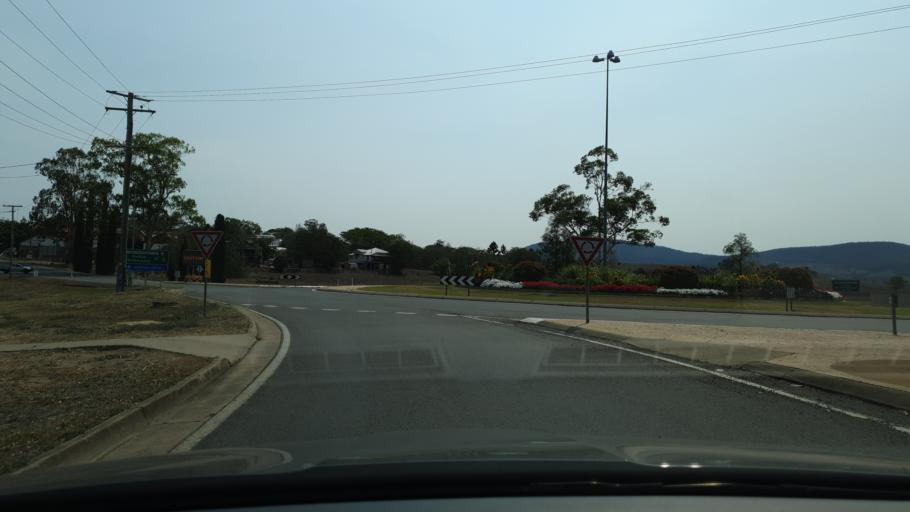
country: AU
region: Queensland
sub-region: Ipswich
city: Deebing Heights
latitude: -27.9936
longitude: 152.6831
